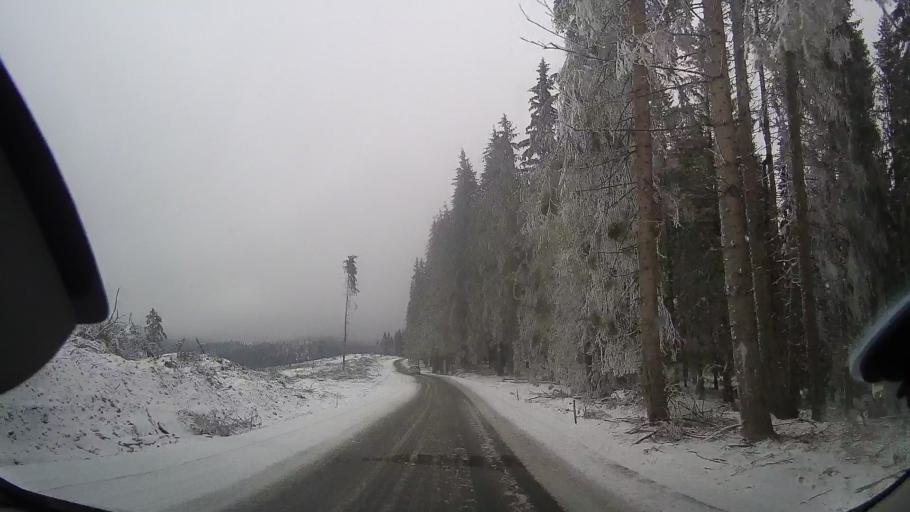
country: RO
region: Cluj
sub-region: Comuna Belis
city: Belis
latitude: 46.6408
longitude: 23.0414
